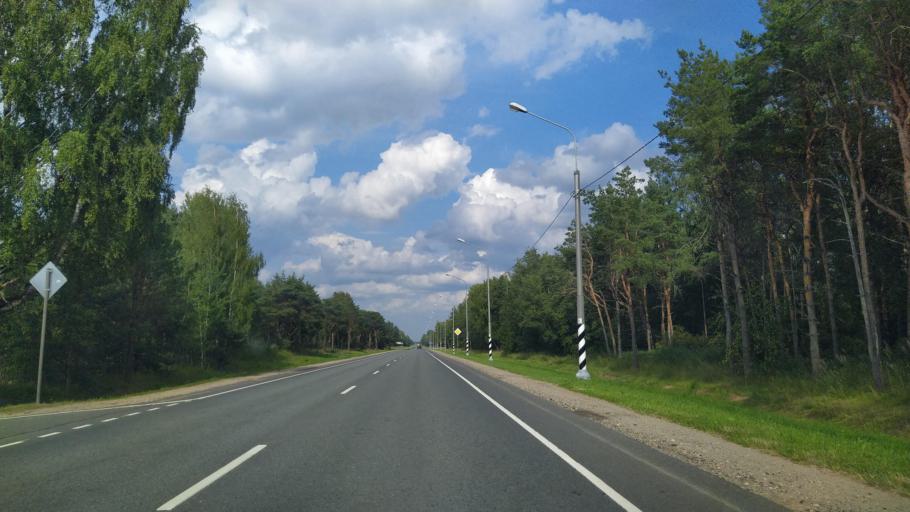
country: RU
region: Novgorod
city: Shimsk
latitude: 58.1800
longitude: 30.5367
